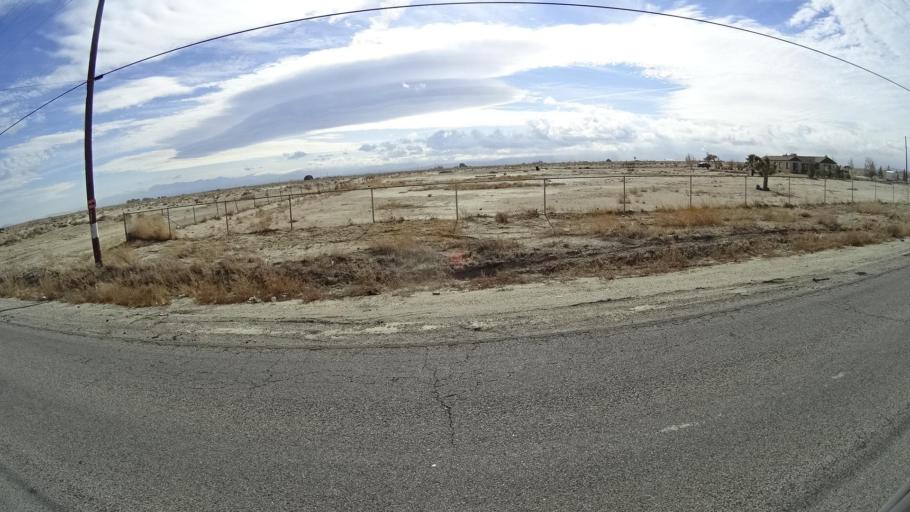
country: US
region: California
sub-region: Kern County
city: Rosamond
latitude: 34.8202
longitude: -118.2115
